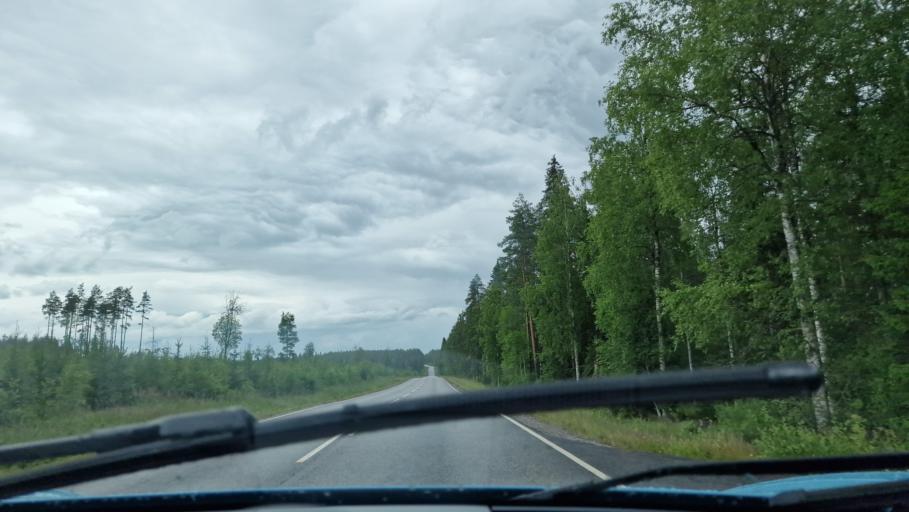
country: FI
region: Central Finland
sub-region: Saarijaervi-Viitasaari
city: Pylkoenmaeki
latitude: 62.6043
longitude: 24.5857
